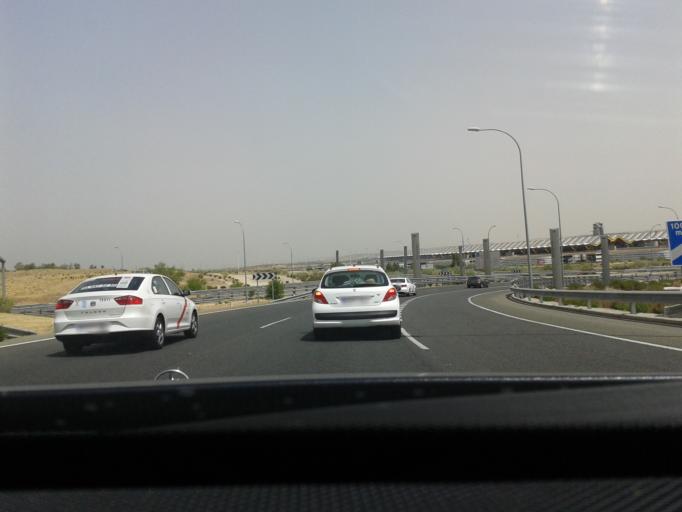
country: ES
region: Madrid
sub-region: Provincia de Madrid
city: Barajas de Madrid
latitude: 40.4860
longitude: -3.6007
